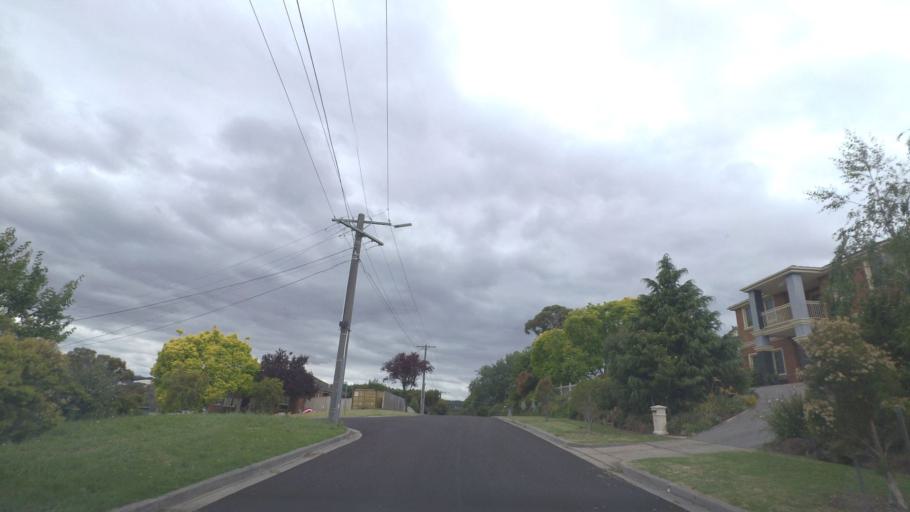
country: AU
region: Victoria
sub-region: Yarra Ranges
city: Lilydale
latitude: -37.7479
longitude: 145.3464
